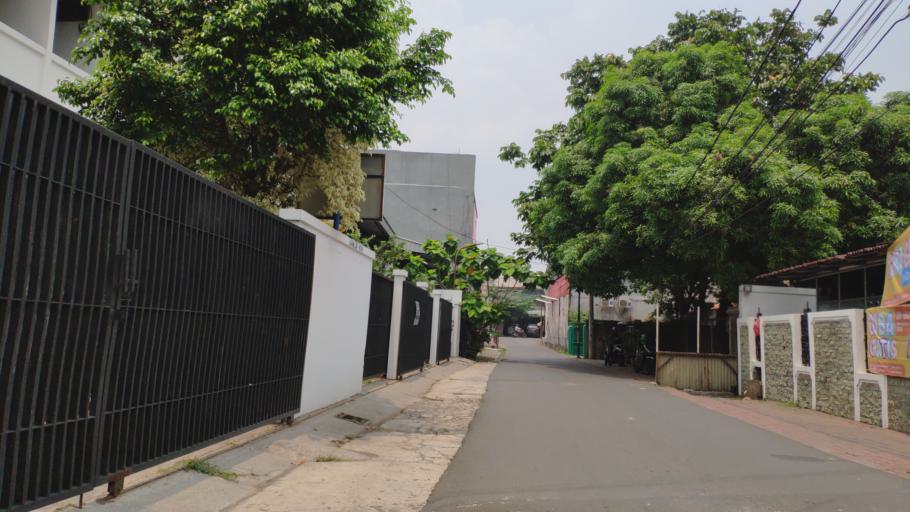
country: ID
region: Banten
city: South Tangerang
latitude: -6.2648
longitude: 106.7670
